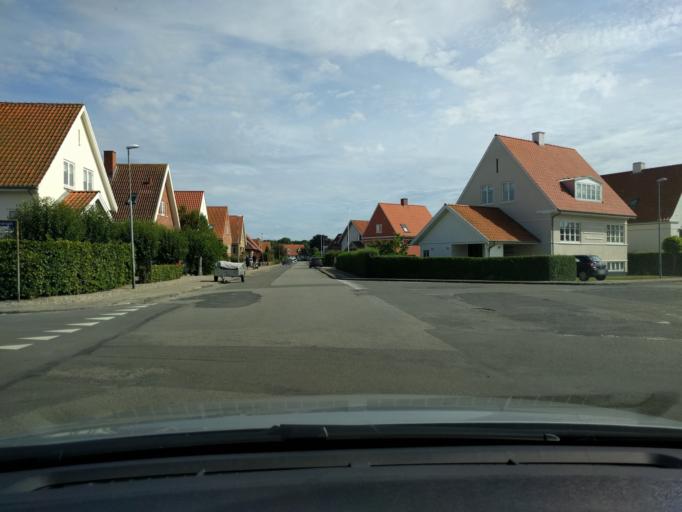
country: DK
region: South Denmark
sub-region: Kerteminde Kommune
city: Kerteminde
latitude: 55.4481
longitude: 10.6637
